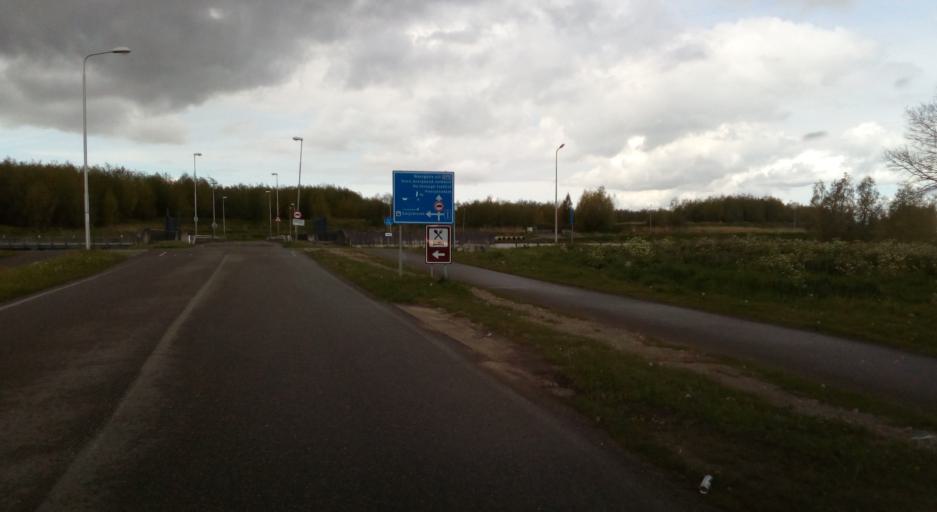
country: NL
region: South Holland
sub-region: Gemeente Zwijndrecht
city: Heerjansdam
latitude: 51.8145
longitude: 4.5885
